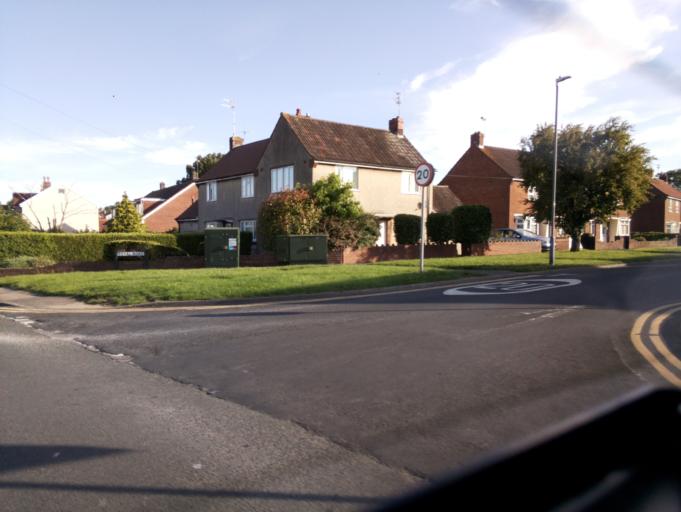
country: GB
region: England
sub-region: South Gloucestershire
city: Mangotsfield
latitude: 51.4868
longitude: -2.4915
